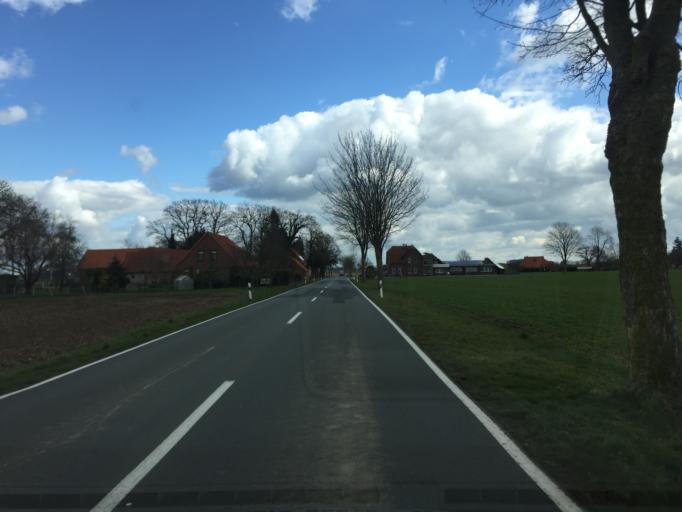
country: DE
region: Lower Saxony
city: Engeln
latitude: 52.7978
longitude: 8.9143
